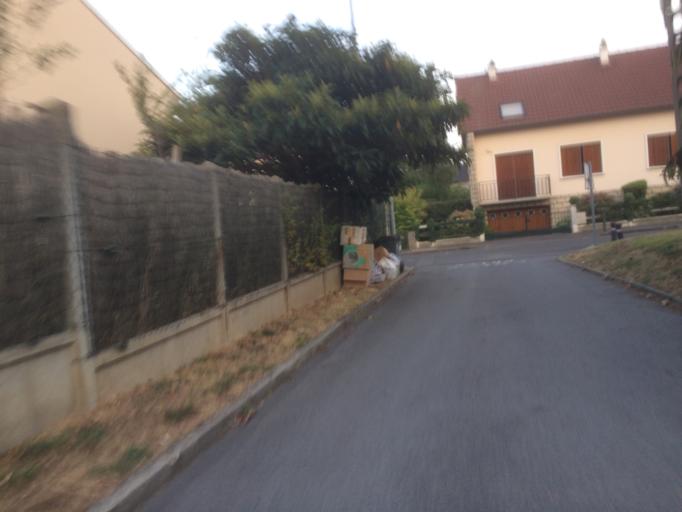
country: FR
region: Ile-de-France
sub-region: Departement de l'Essonne
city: Palaiseau
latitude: 48.7275
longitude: 2.2532
